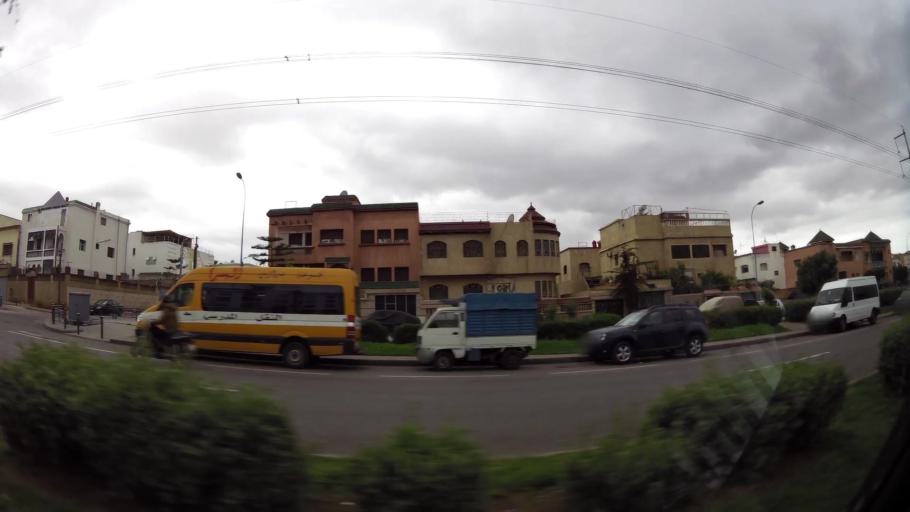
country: MA
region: Grand Casablanca
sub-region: Mediouna
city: Tit Mellil
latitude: 33.5670
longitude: -7.5311
